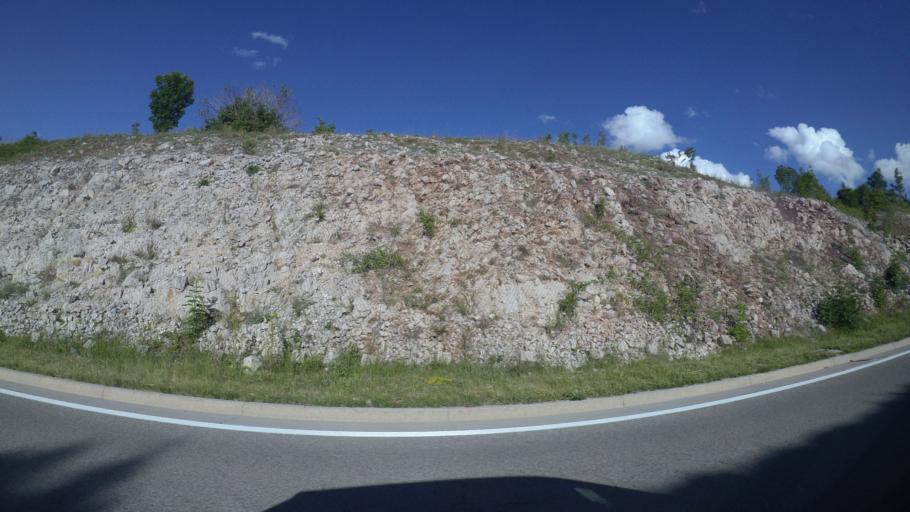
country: HR
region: Zadarska
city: Gracac
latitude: 44.5319
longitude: 15.7498
